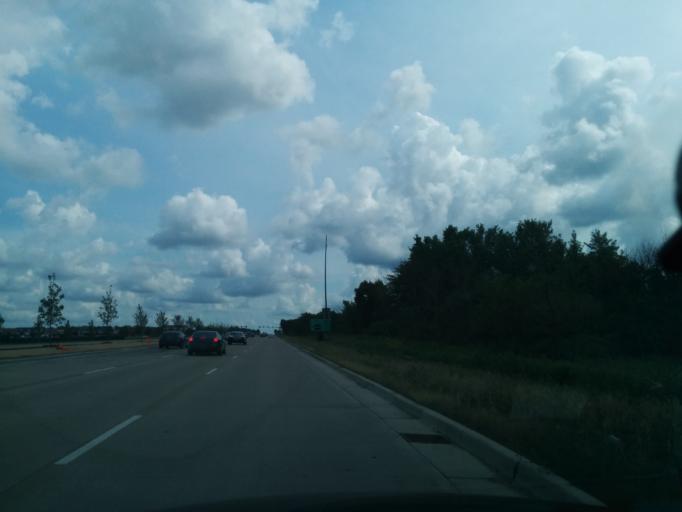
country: US
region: Illinois
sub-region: Cook County
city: Orland Hills
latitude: 41.5835
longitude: -87.8523
